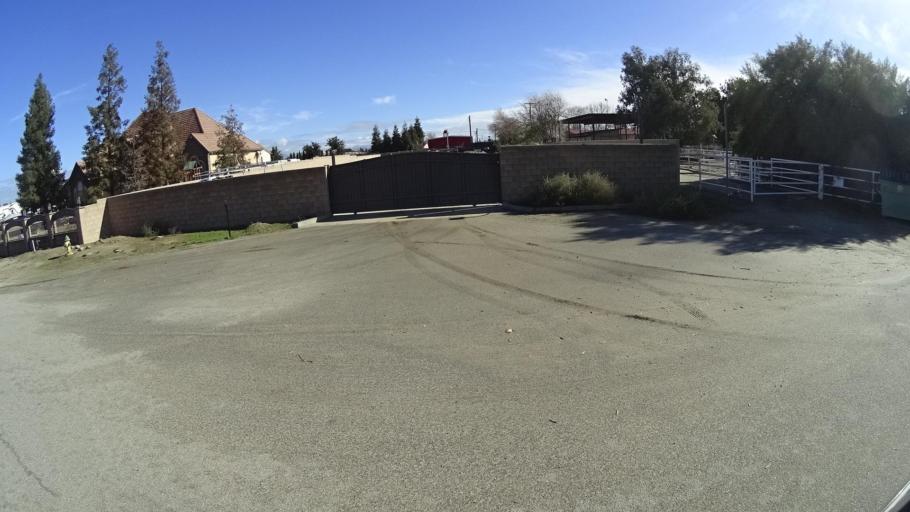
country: US
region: California
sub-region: Kern County
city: Rosedale
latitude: 35.3581
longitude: -119.2078
